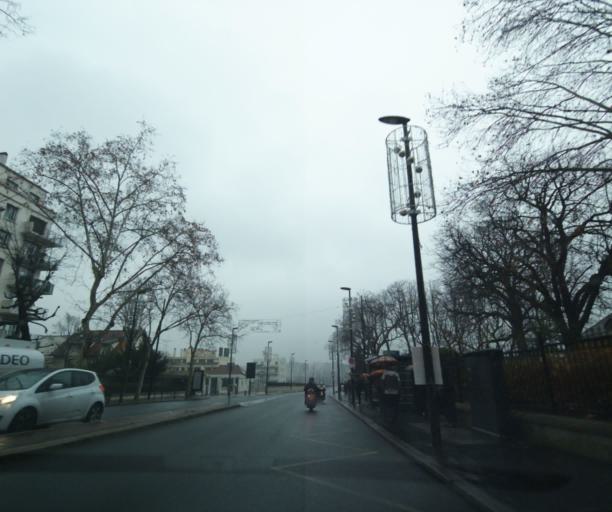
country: FR
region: Ile-de-France
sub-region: Departement des Hauts-de-Seine
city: Levallois-Perret
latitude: 48.9024
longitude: 2.2748
